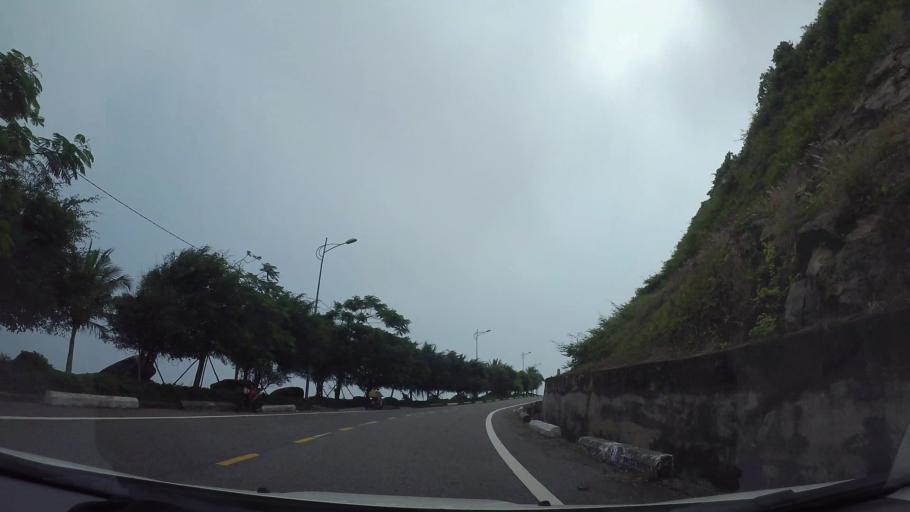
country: VN
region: Da Nang
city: Son Tra
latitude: 16.1031
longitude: 108.3080
